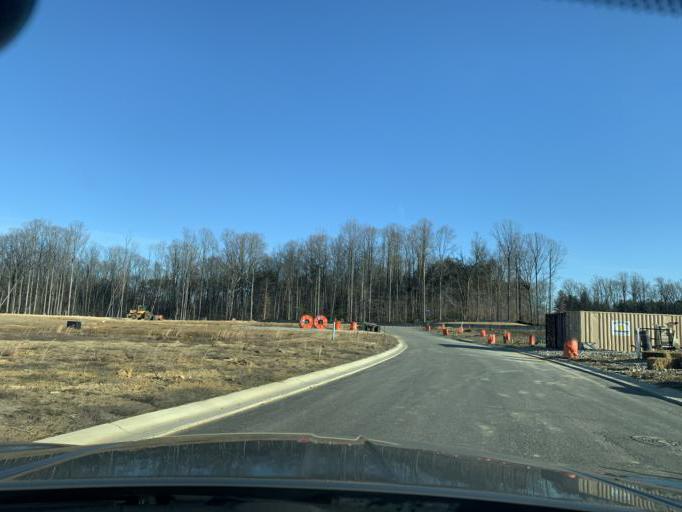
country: US
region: Maryland
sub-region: Anne Arundel County
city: Crofton
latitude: 39.0197
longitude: -76.7209
